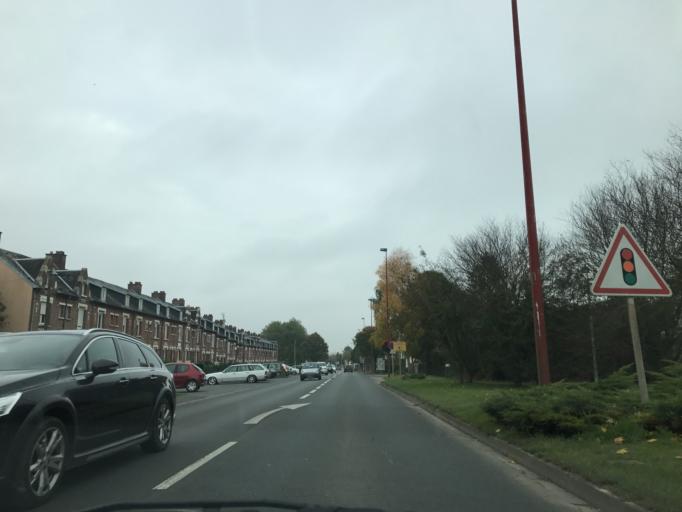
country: FR
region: Picardie
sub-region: Departement de la Somme
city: Peronne
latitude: 49.9097
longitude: 2.9322
